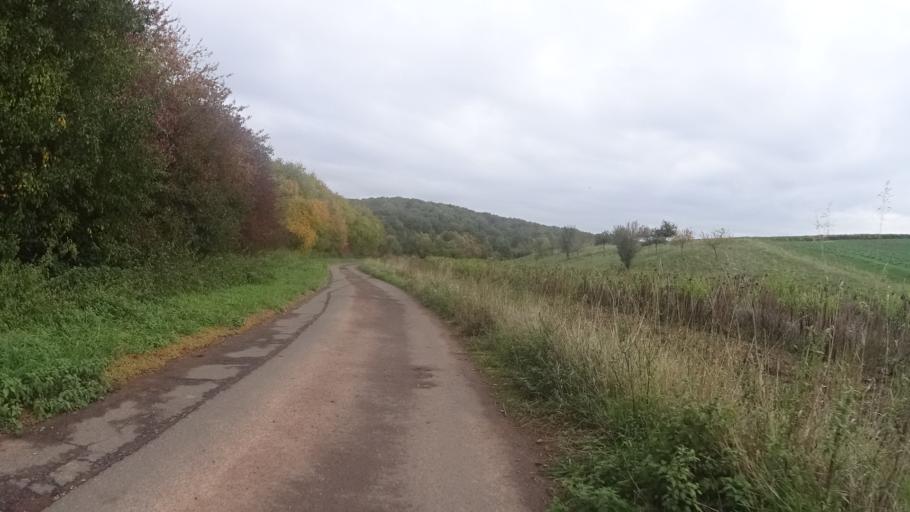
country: DE
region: Rheinland-Pfalz
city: Bennhausen
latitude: 49.6270
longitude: 7.9913
